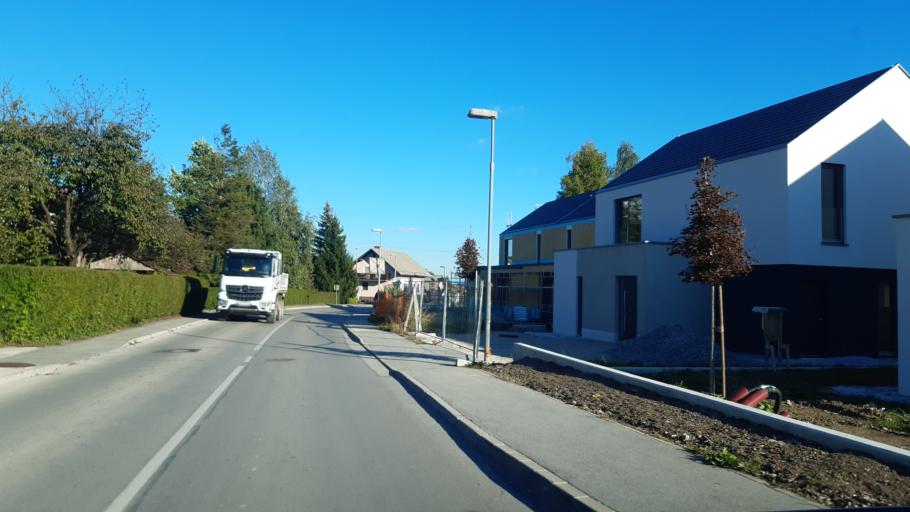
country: SI
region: Kranj
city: Zgornje Bitnje
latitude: 46.2291
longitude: 14.3380
